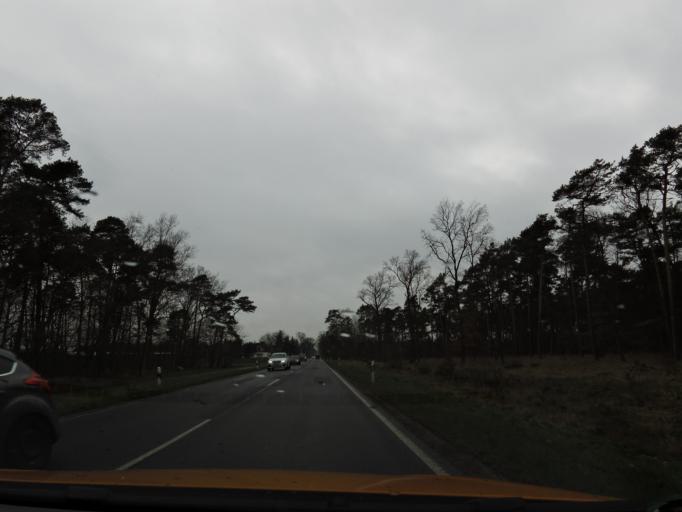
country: DE
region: Brandenburg
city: Gross Kreutz
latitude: 52.4064
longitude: 12.7428
